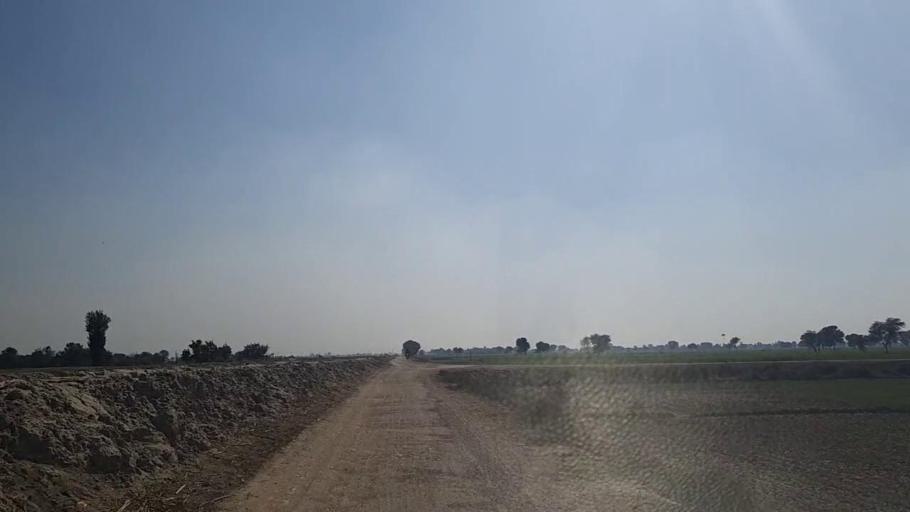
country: PK
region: Sindh
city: Shahpur Chakar
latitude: 26.2149
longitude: 68.5839
